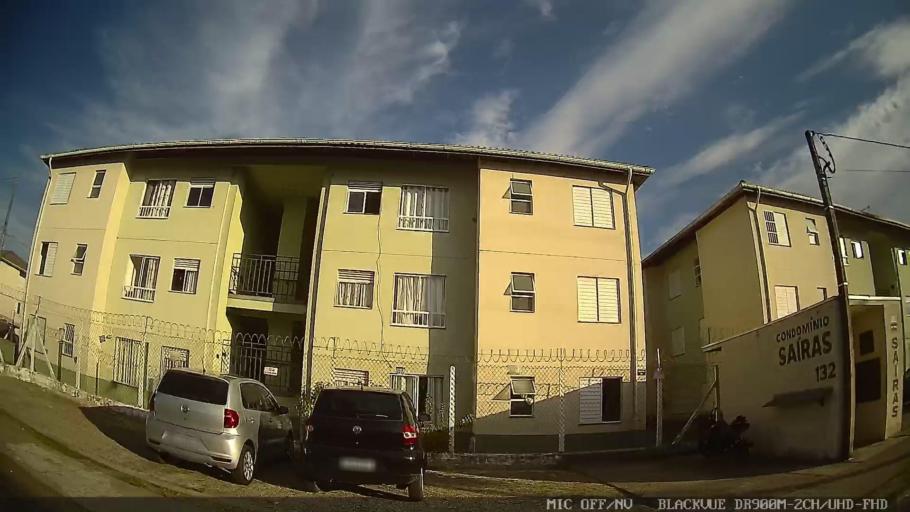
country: BR
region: Sao Paulo
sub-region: Itanhaem
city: Itanhaem
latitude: -24.1505
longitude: -46.7972
